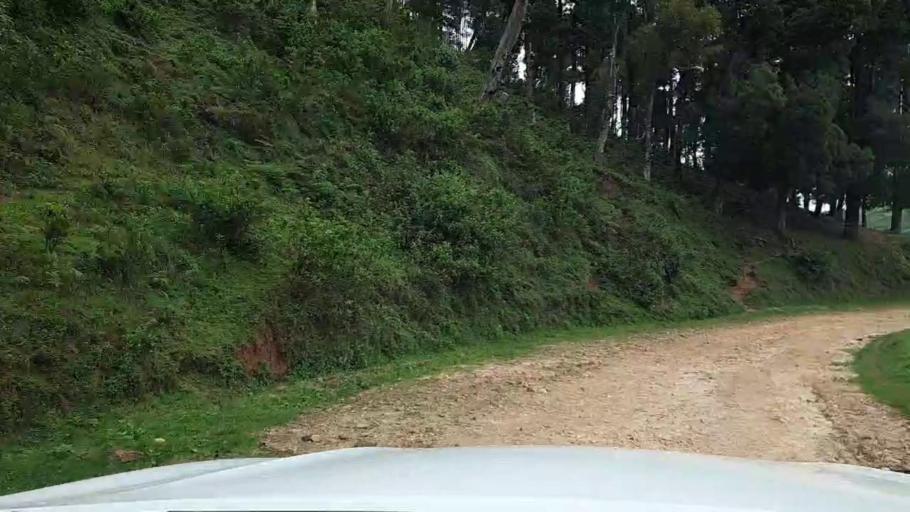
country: RW
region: Western Province
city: Kibuye
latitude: -2.2891
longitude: 29.3681
